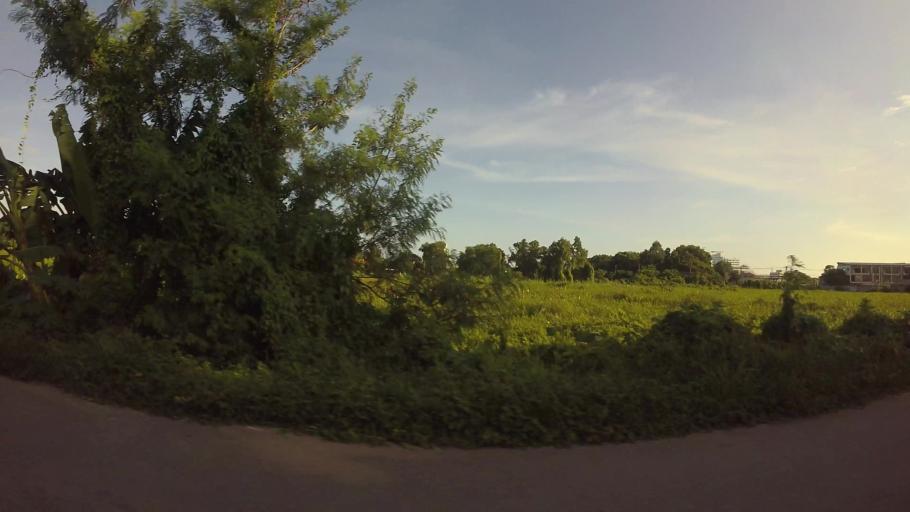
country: TH
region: Rayong
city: Rayong
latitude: 12.6884
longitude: 101.2818
